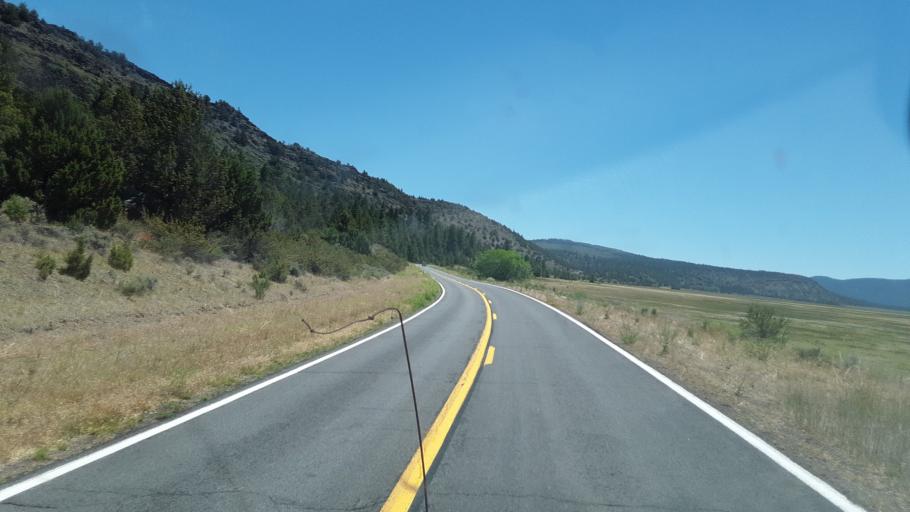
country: US
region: California
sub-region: Lassen County
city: Susanville
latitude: 40.6736
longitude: -120.6577
